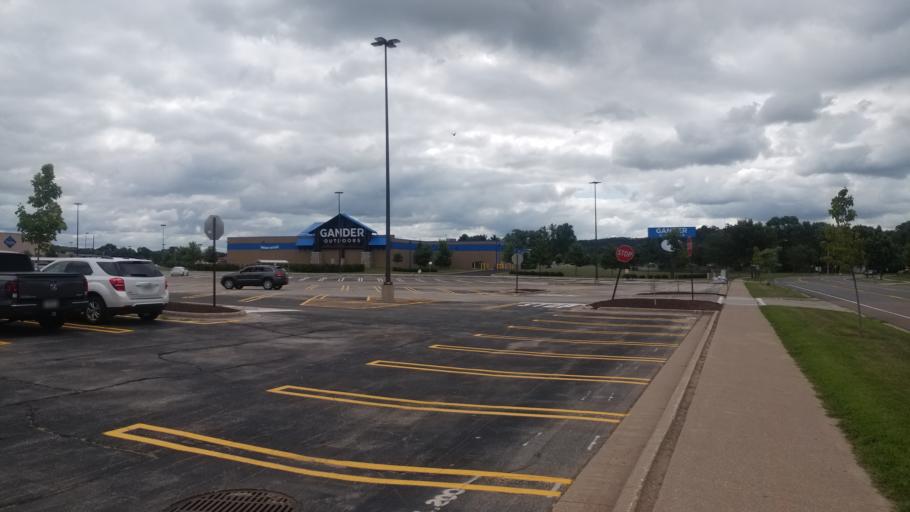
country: US
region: Wisconsin
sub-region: La Crosse County
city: Onalaska
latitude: 43.8703
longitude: -91.2178
